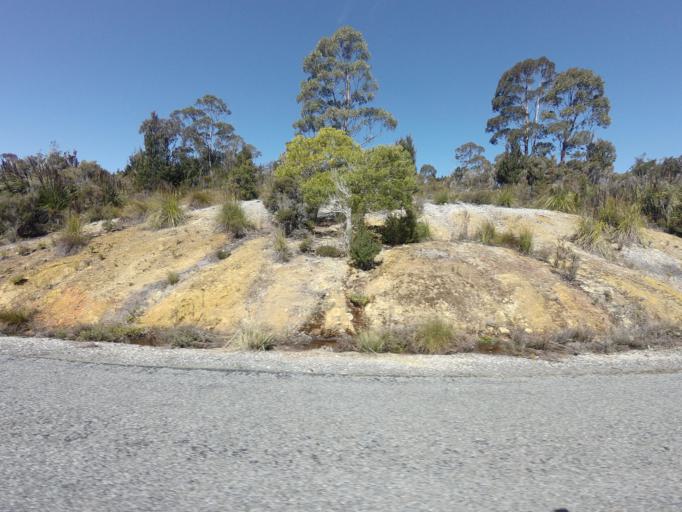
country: AU
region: Tasmania
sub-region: Derwent Valley
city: New Norfolk
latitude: -42.7605
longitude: 146.3970
